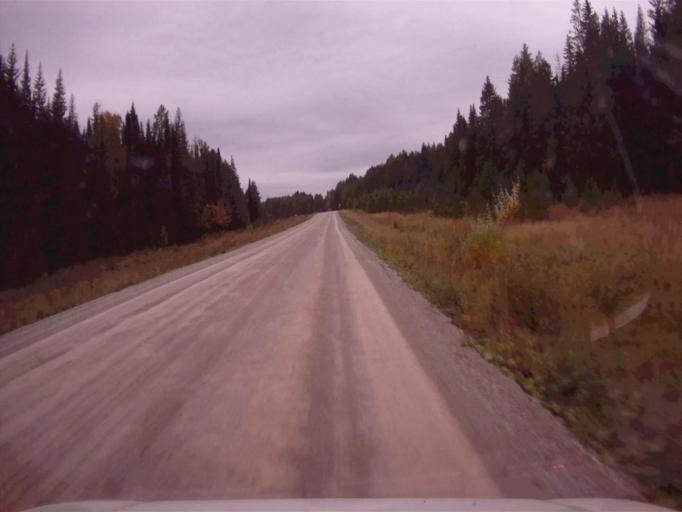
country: RU
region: Chelyabinsk
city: Nyazepetrovsk
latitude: 56.0544
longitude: 59.5426
